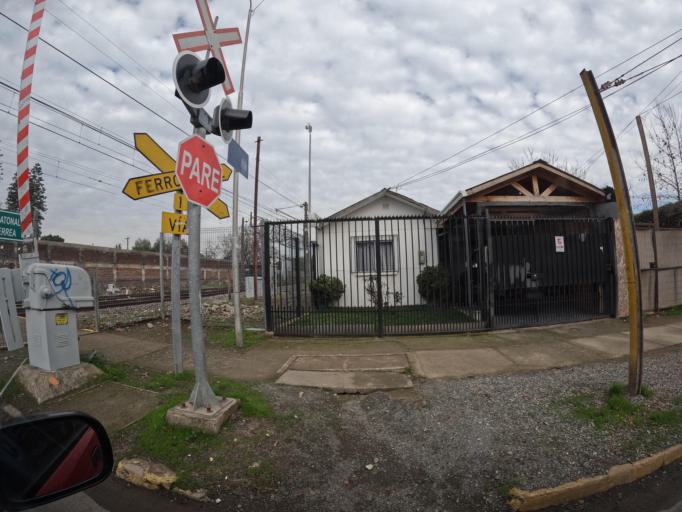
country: CL
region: Maule
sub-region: Provincia de Linares
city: Linares
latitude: -35.8500
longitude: -71.5916
